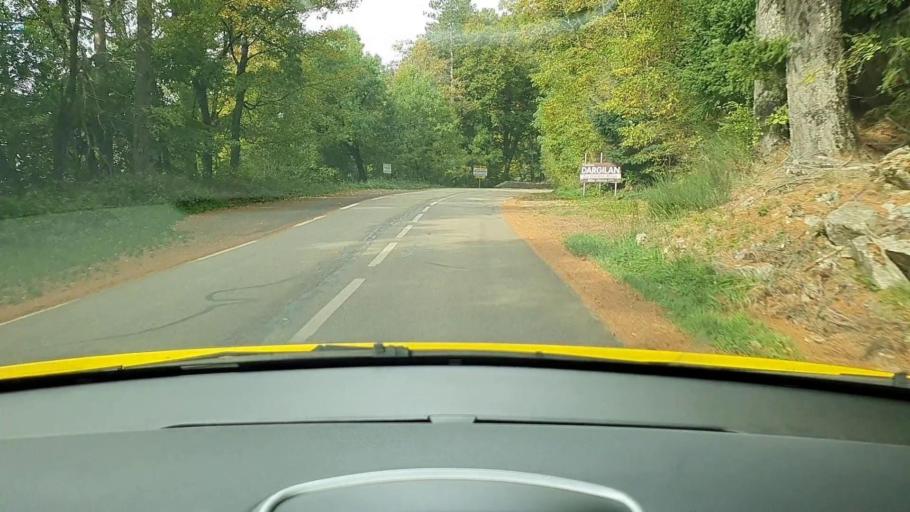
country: FR
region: Languedoc-Roussillon
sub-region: Departement de la Lozere
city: Meyrueis
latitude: 44.1234
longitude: 3.4776
